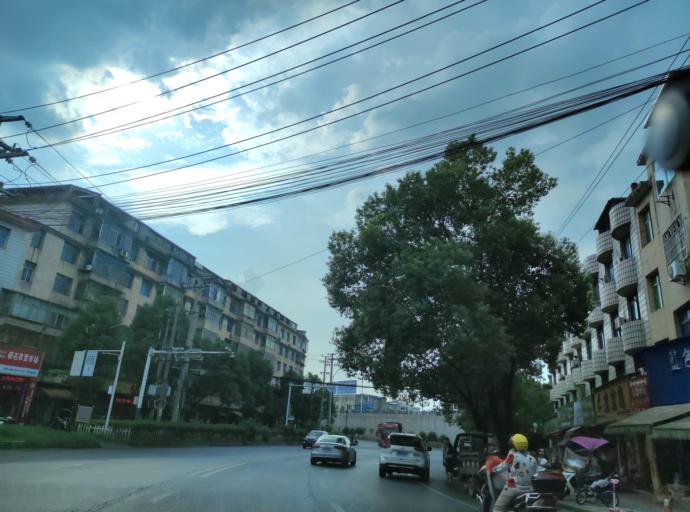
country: CN
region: Jiangxi Sheng
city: Pingxiang
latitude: 27.6617
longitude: 113.8366
